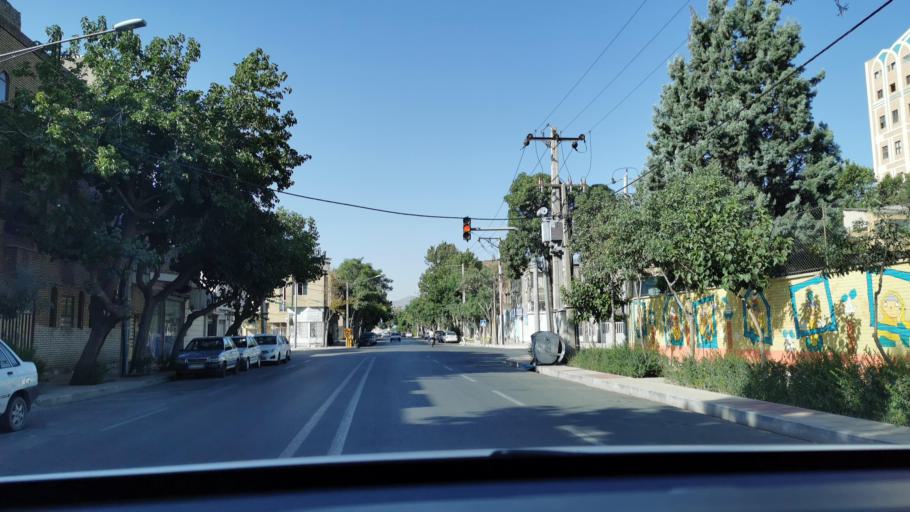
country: IR
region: Razavi Khorasan
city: Mashhad
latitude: 36.3013
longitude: 59.6217
